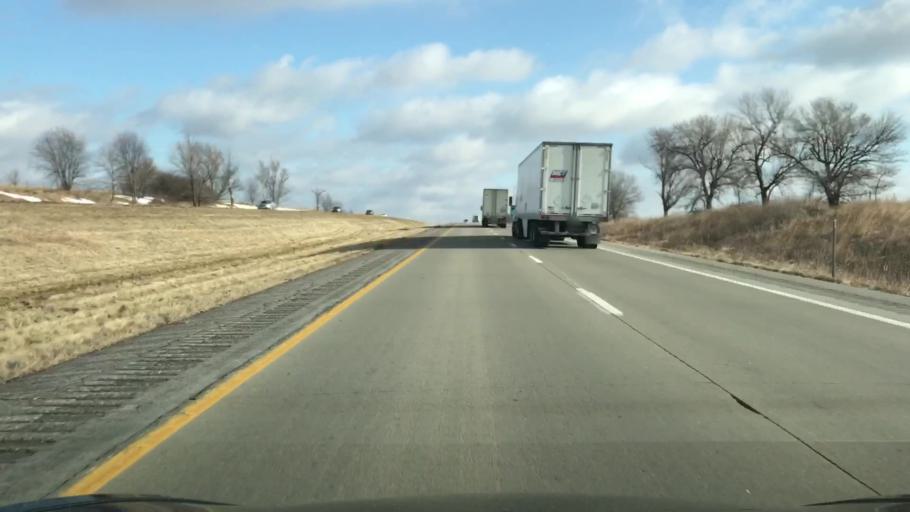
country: US
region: Iowa
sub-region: Cass County
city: Atlantic
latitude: 41.4971
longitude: -94.9732
